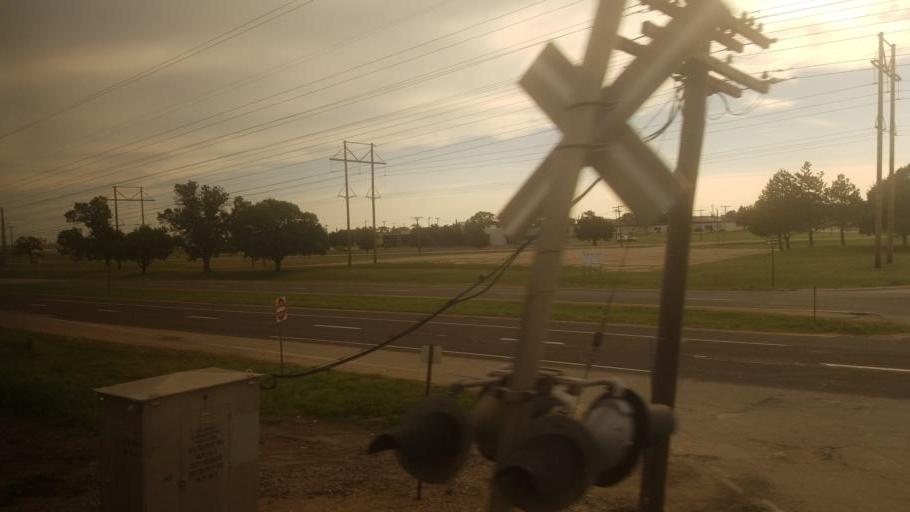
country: US
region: Kansas
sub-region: Shawnee County
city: Topeka
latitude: 38.9467
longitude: -95.6876
